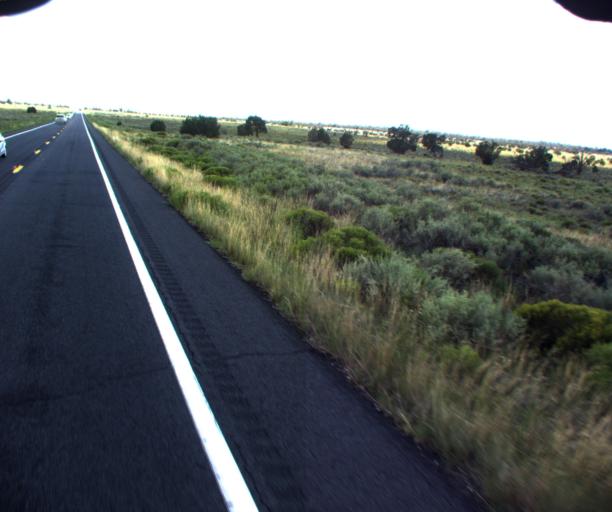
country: US
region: Arizona
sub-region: Coconino County
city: Grand Canyon Village
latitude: 35.6865
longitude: -112.1348
